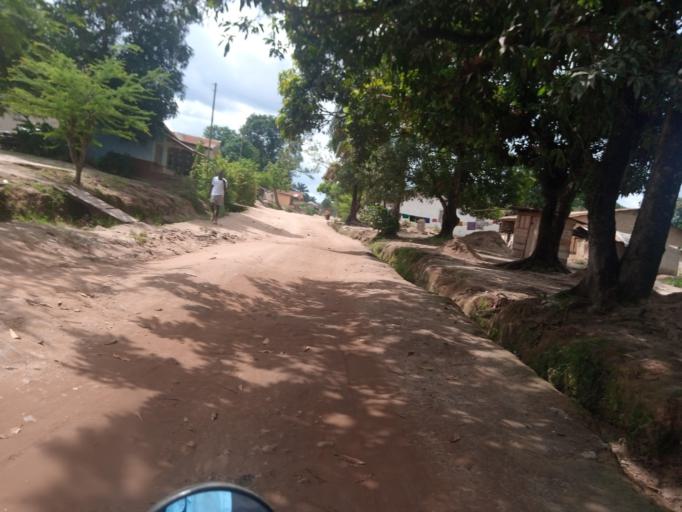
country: SL
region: Southern Province
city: Bo
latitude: 7.9780
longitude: -11.7319
